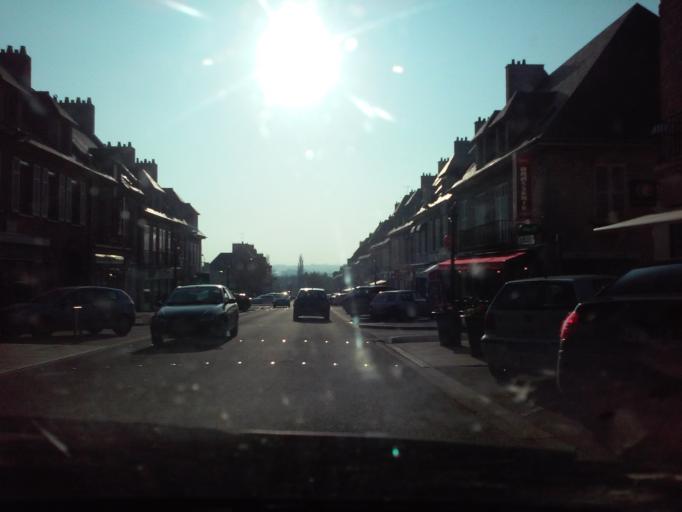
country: FR
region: Lower Normandy
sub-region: Departement du Calvados
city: Villers-Bocage
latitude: 49.0805
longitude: -0.6565
